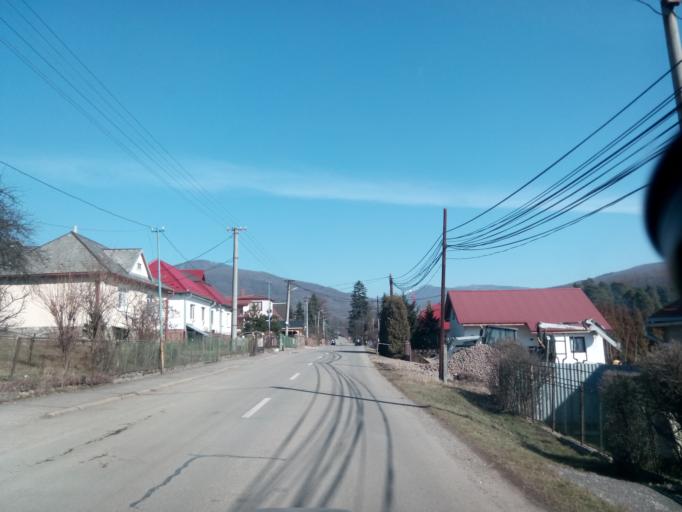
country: SK
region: Kosicky
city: Sobrance
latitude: 48.8465
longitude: 22.1833
